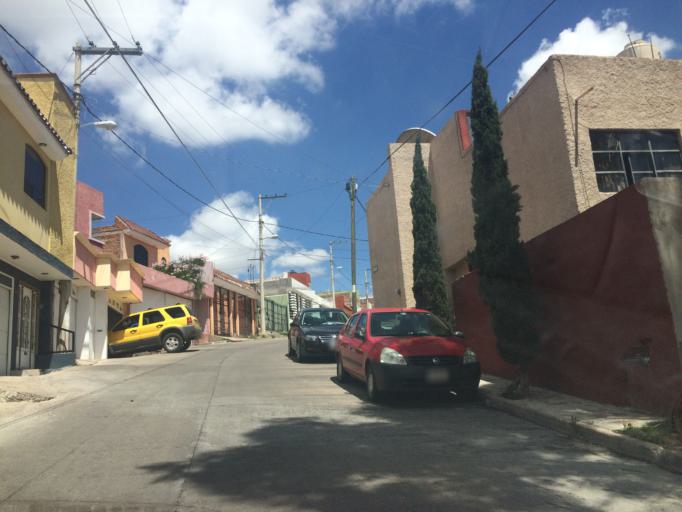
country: MX
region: Zacatecas
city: Zacatecas
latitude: 22.7558
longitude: -102.5780
